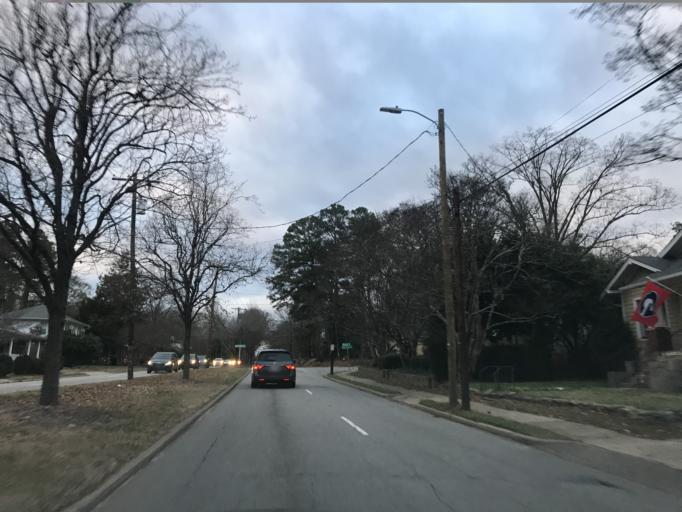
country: US
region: North Carolina
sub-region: Wake County
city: West Raleigh
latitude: 35.8074
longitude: -78.6478
